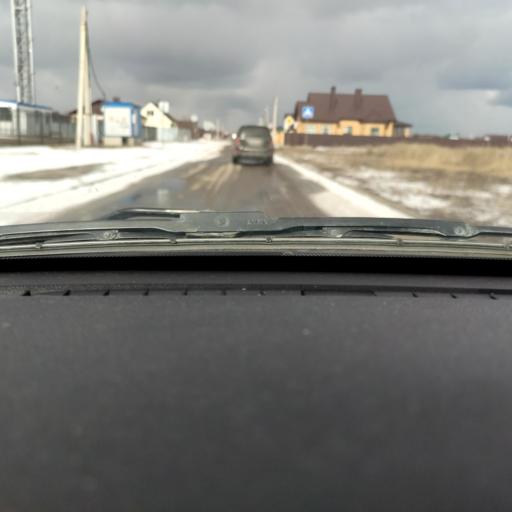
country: RU
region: Voronezj
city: Novaya Usman'
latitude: 51.6607
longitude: 39.4547
